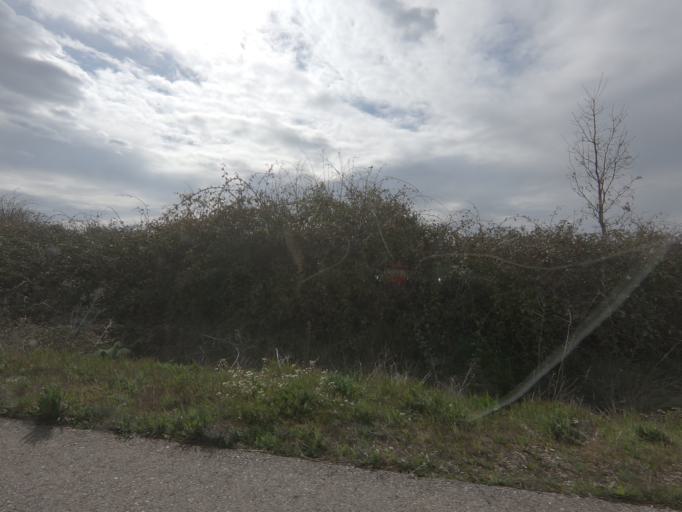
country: ES
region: Castille and Leon
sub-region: Provincia de Salamanca
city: Robleda
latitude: 40.4243
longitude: -6.5995
